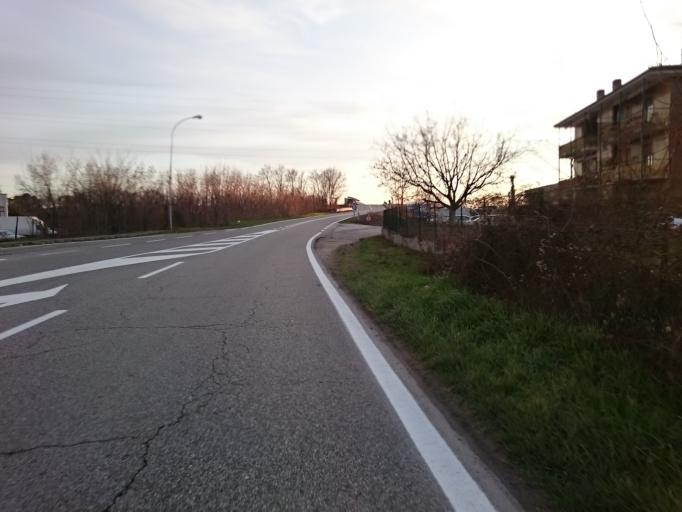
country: IT
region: Veneto
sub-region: Provincia di Verona
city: Castelnuovo del Garda
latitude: 45.4286
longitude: 10.7573
